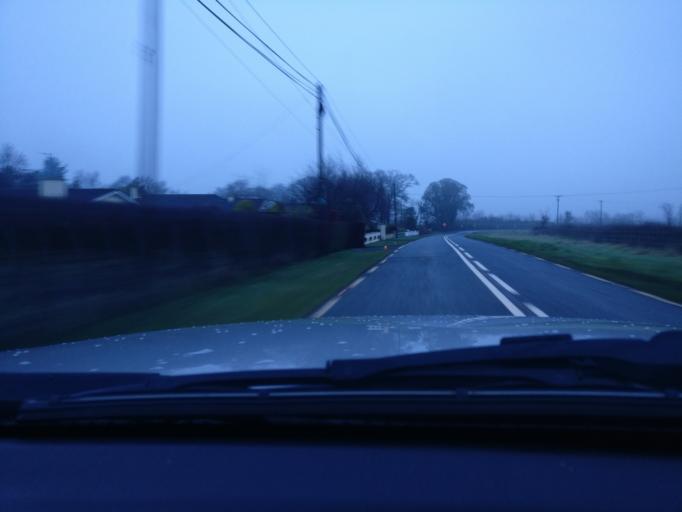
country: IE
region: Leinster
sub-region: An Mhi
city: Athboy
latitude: 53.6093
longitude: -6.9638
